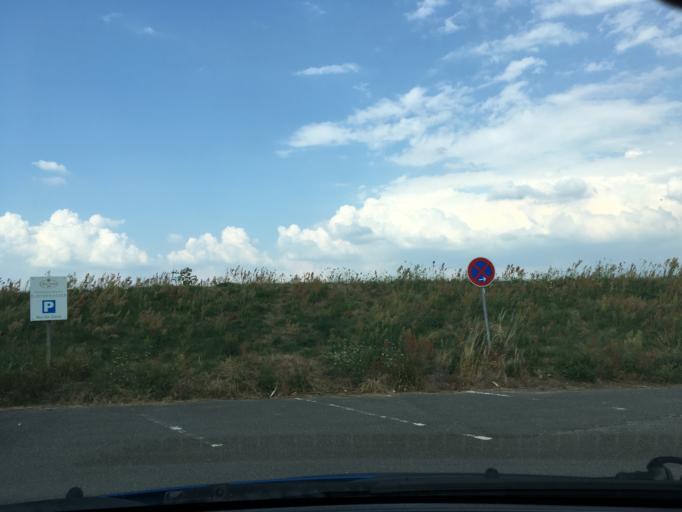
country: DE
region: Lower Saxony
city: Hitzacker
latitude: 53.1372
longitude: 11.0815
